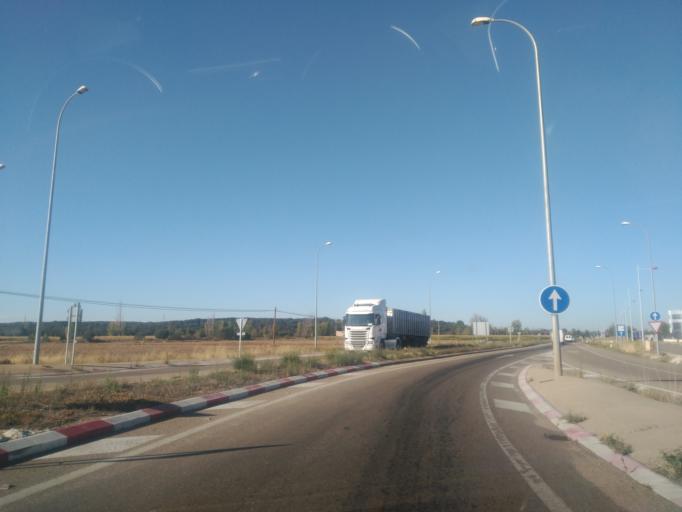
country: ES
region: Castille and Leon
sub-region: Provincia de Burgos
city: Villalba de Duero
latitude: 41.6645
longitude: -3.7296
